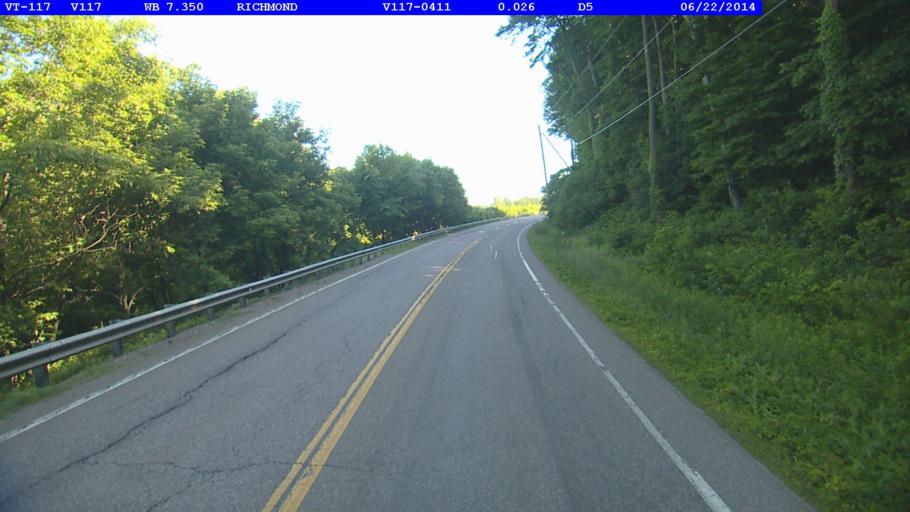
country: US
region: Vermont
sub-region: Chittenden County
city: Williston
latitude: 44.4341
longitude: -73.0210
